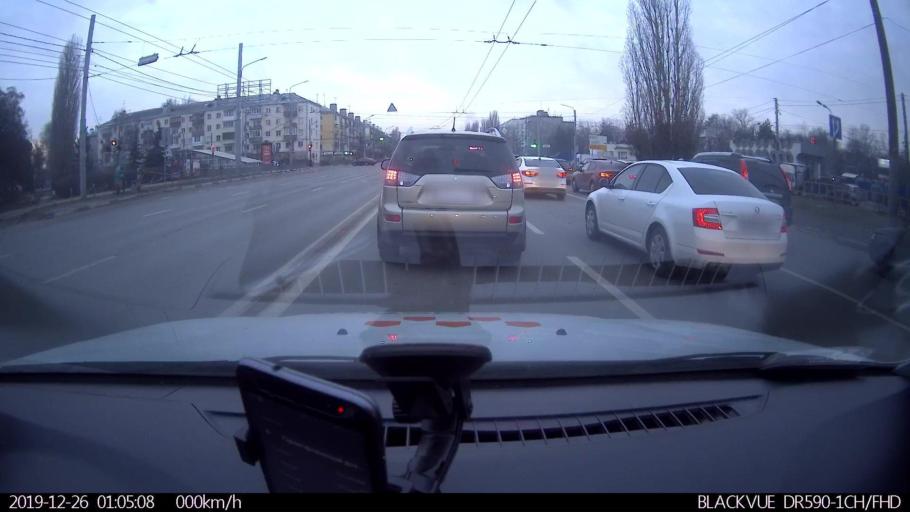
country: RU
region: Nizjnij Novgorod
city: Nizhniy Novgorod
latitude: 56.2851
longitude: 43.9278
